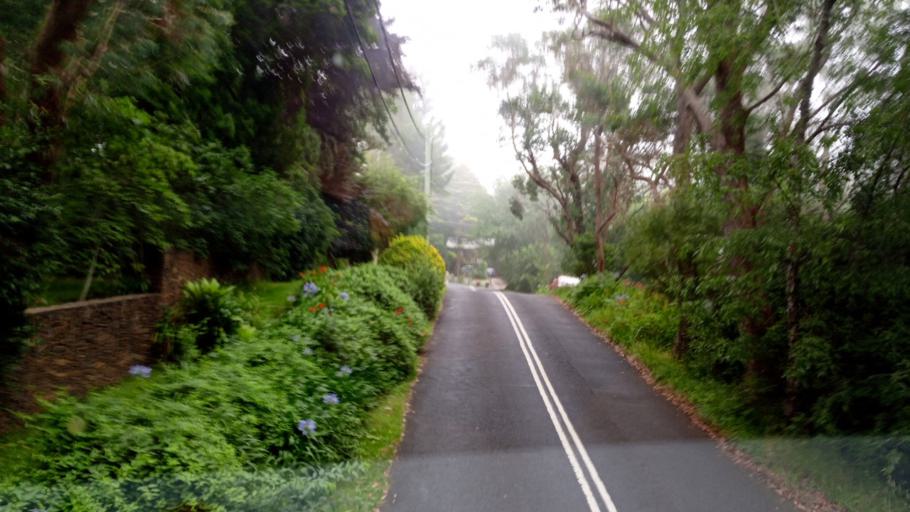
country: AU
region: New South Wales
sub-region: Blue Mountains Municipality
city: Leura
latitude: -33.7177
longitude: 150.3392
